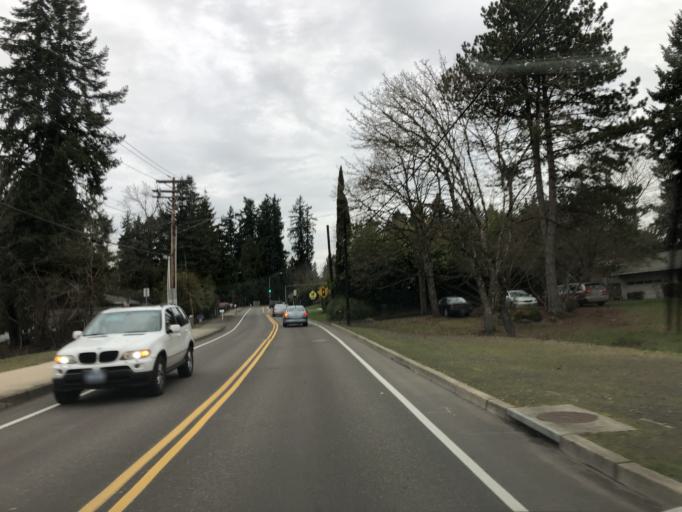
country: US
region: Oregon
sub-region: Washington County
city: Tigard
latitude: 45.4296
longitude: -122.7843
